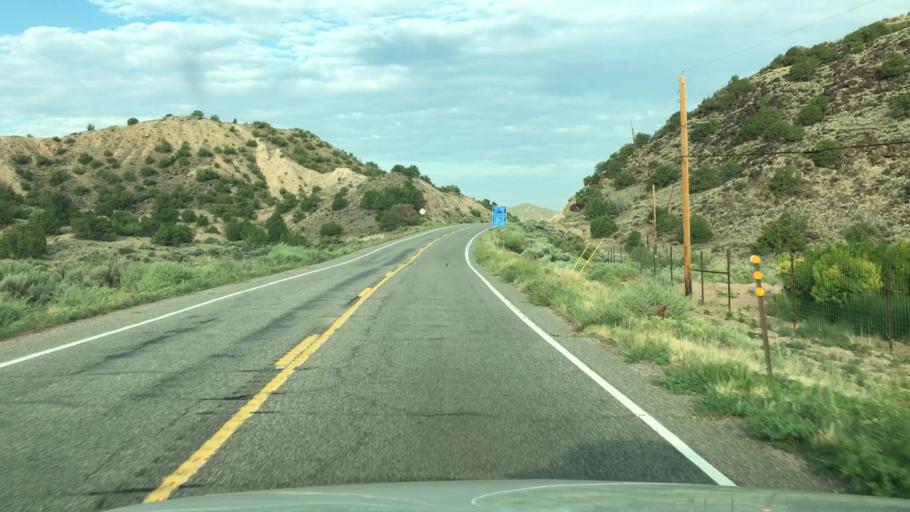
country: US
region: New Mexico
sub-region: Rio Arriba County
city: Chimayo
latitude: 36.2151
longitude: -105.8854
